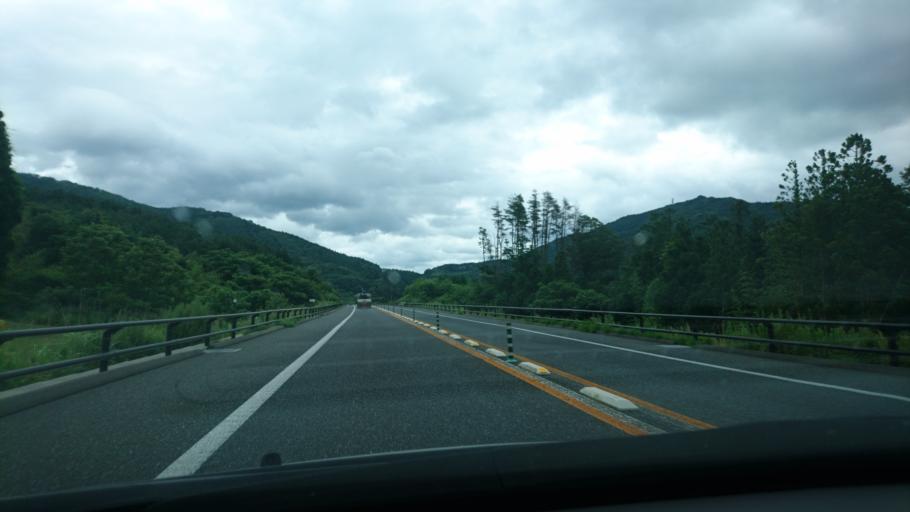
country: JP
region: Iwate
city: Ofunato
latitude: 39.0264
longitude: 141.6714
